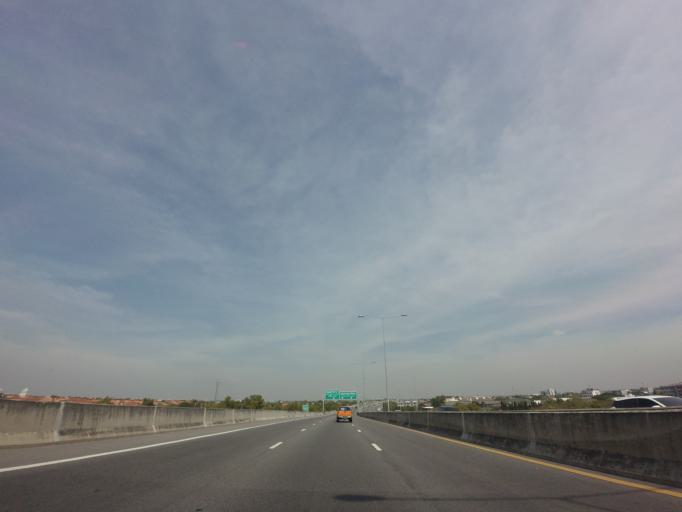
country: TH
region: Bangkok
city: Bang Khen
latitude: 13.8767
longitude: 100.6468
